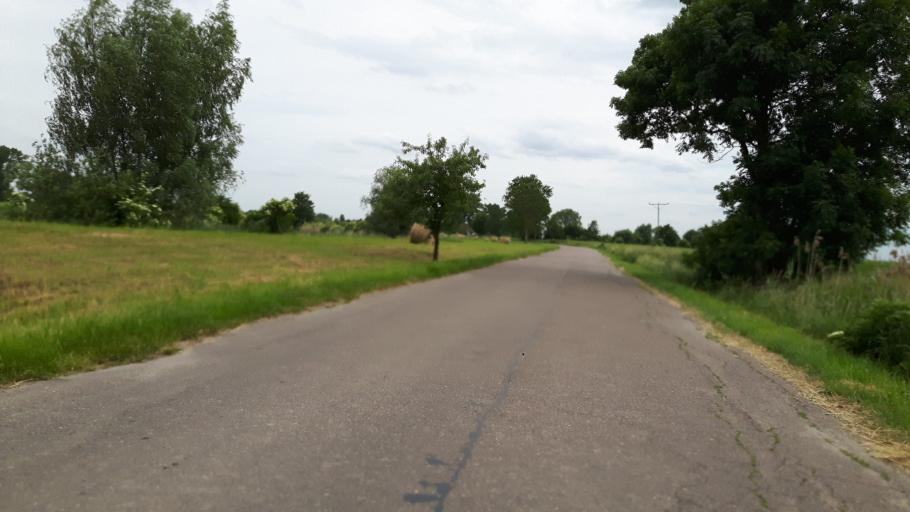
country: PL
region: Pomeranian Voivodeship
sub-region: Powiat nowodworski
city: Sztutowo
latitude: 54.2479
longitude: 19.2381
